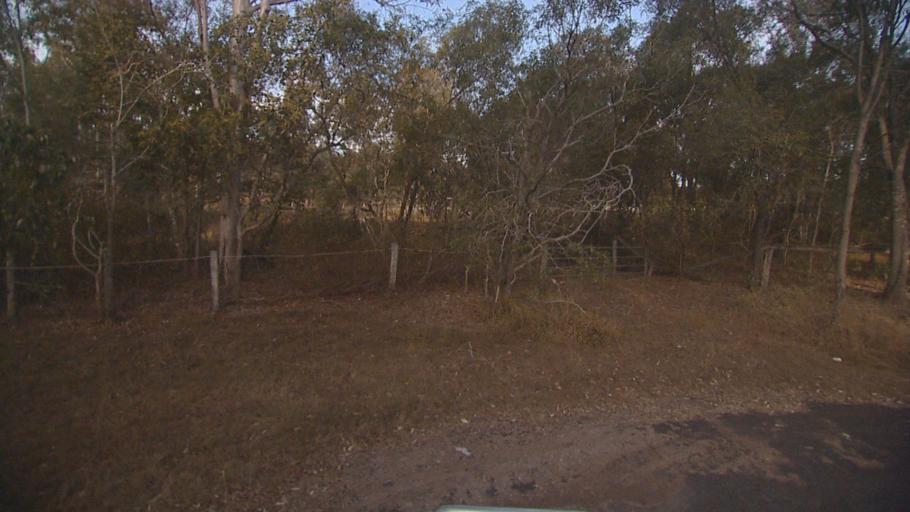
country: AU
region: Queensland
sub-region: Logan
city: Cedar Vale
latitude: -27.8536
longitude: 153.0584
